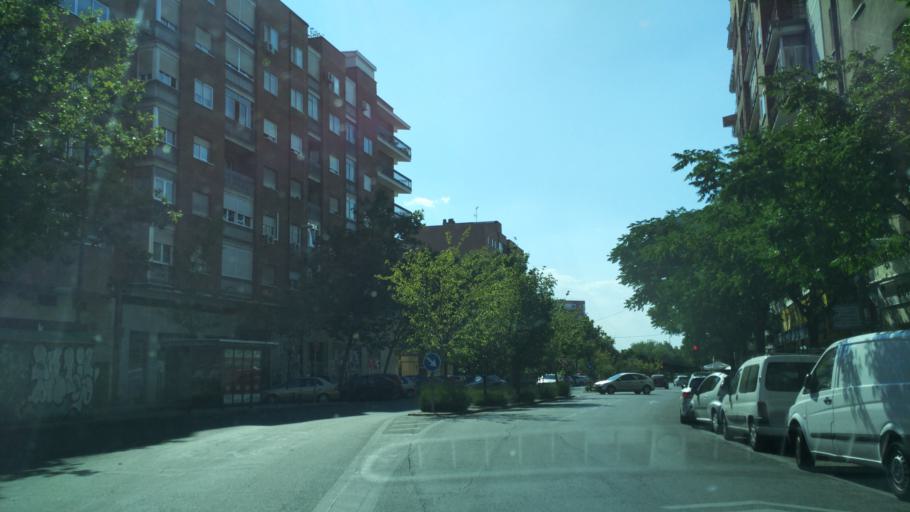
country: ES
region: Madrid
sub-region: Provincia de Madrid
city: Tetuan de las Victorias
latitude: 40.4567
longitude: -3.7078
